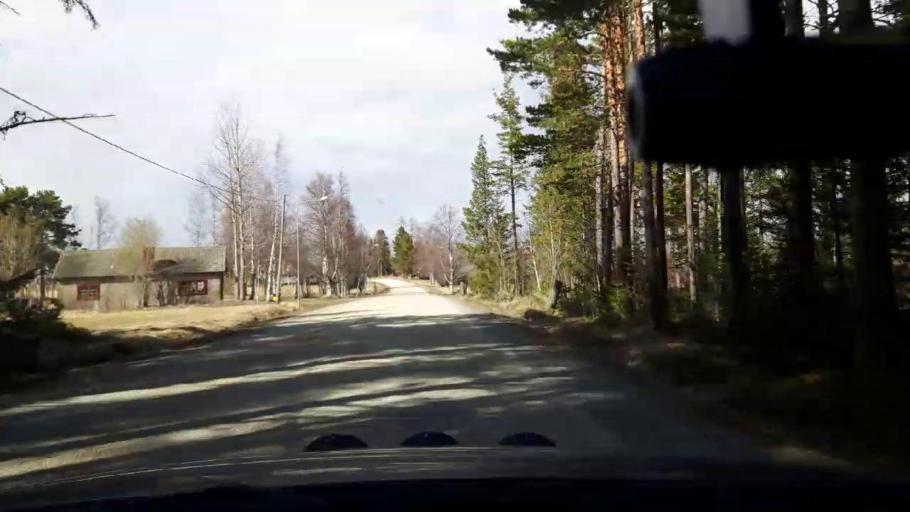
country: SE
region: Jaemtland
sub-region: Bergs Kommun
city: Hoverberg
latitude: 62.9065
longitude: 14.3401
